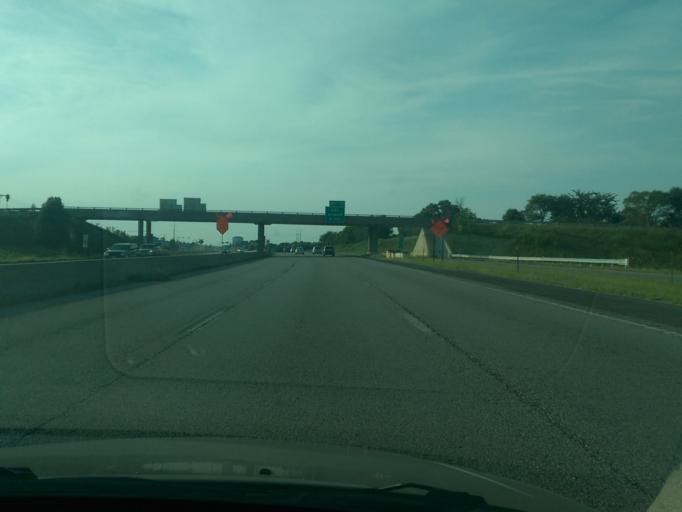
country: US
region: Missouri
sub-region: Platte County
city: Weatherby Lake
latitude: 39.2591
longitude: -94.6593
